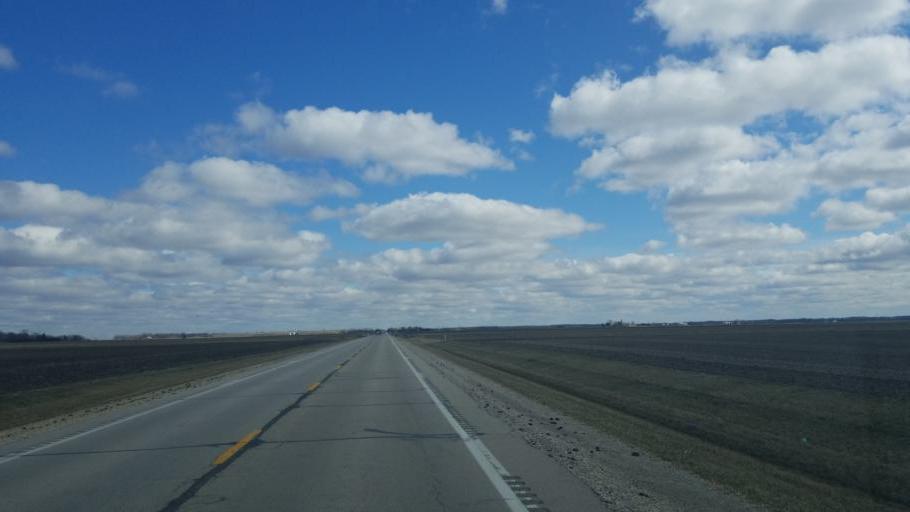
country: US
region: Illinois
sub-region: Douglas County
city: Villa Grove
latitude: 39.7920
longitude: -88.0929
